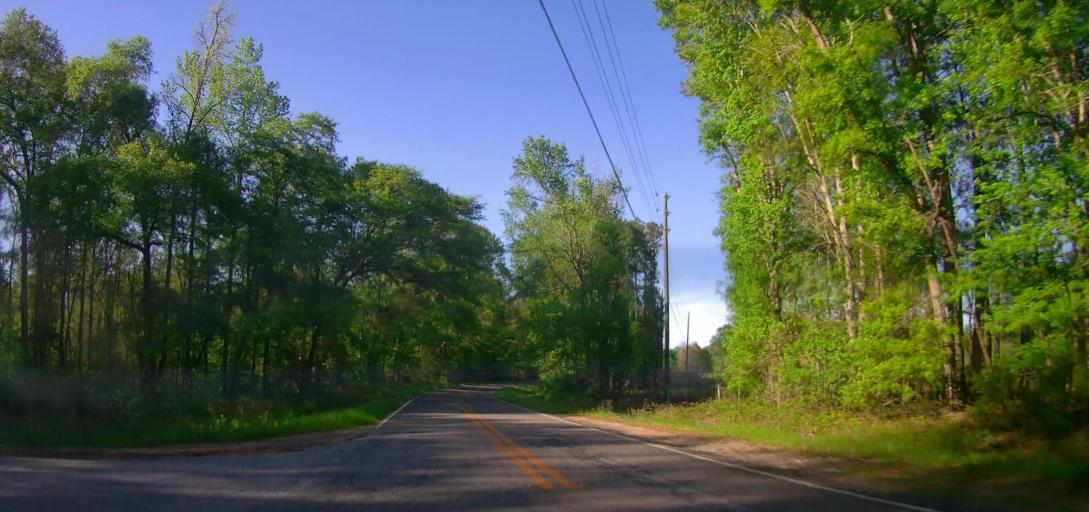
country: US
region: Georgia
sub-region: Houston County
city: Perry
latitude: 32.4612
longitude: -83.8169
